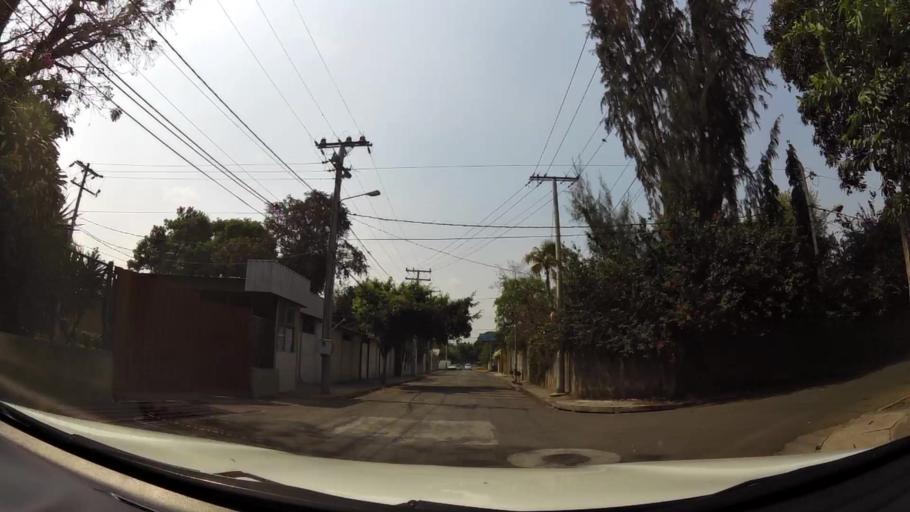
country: NI
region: Managua
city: Ciudad Sandino
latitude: 12.1309
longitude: -86.3141
